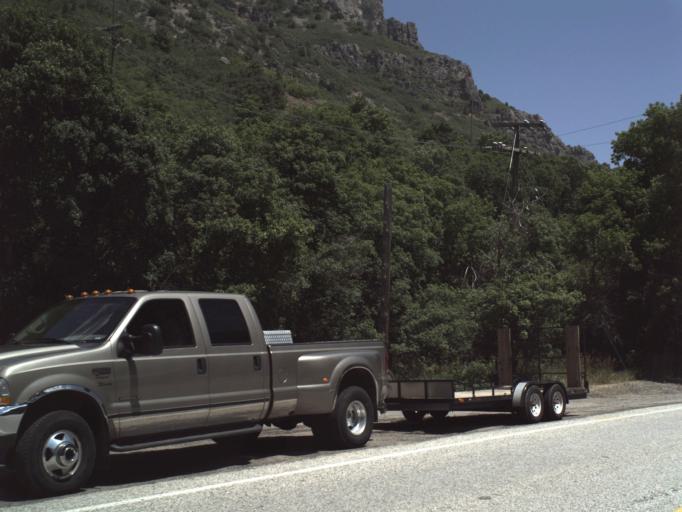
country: US
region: Utah
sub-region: Weber County
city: Liberty
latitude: 41.2550
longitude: -111.8651
